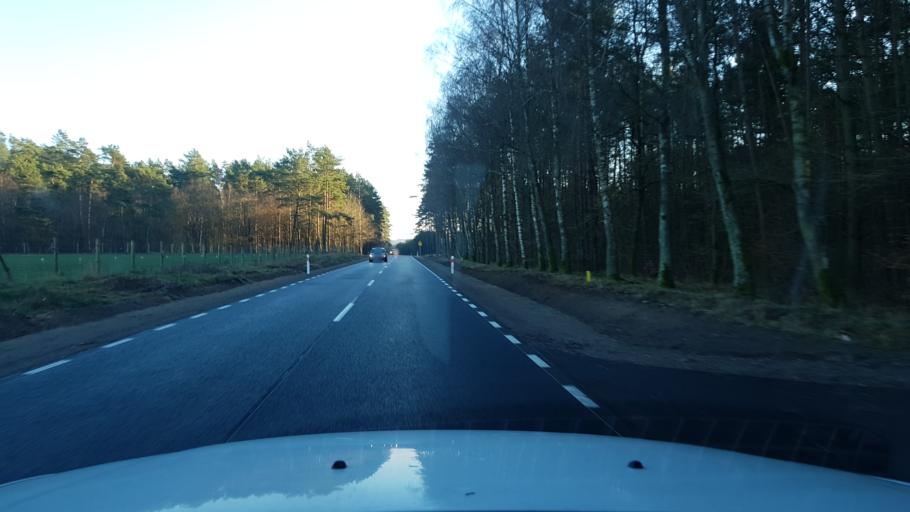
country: PL
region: West Pomeranian Voivodeship
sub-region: Powiat gryficki
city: Brojce
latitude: 53.9487
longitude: 15.3874
